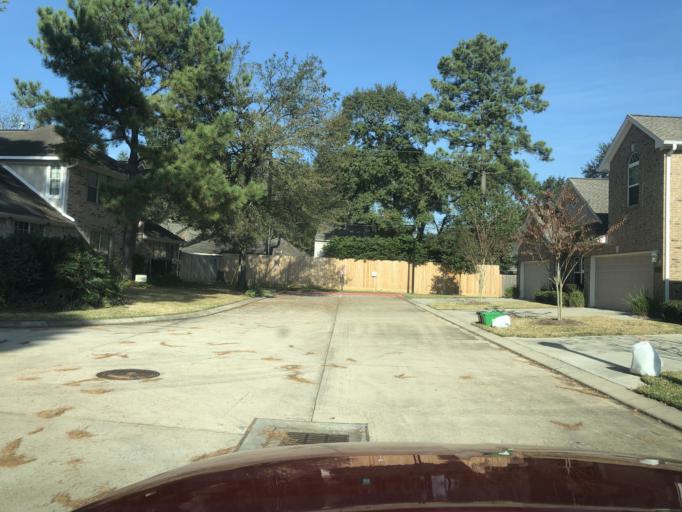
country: US
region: Texas
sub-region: Harris County
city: Spring
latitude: 30.0128
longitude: -95.4621
